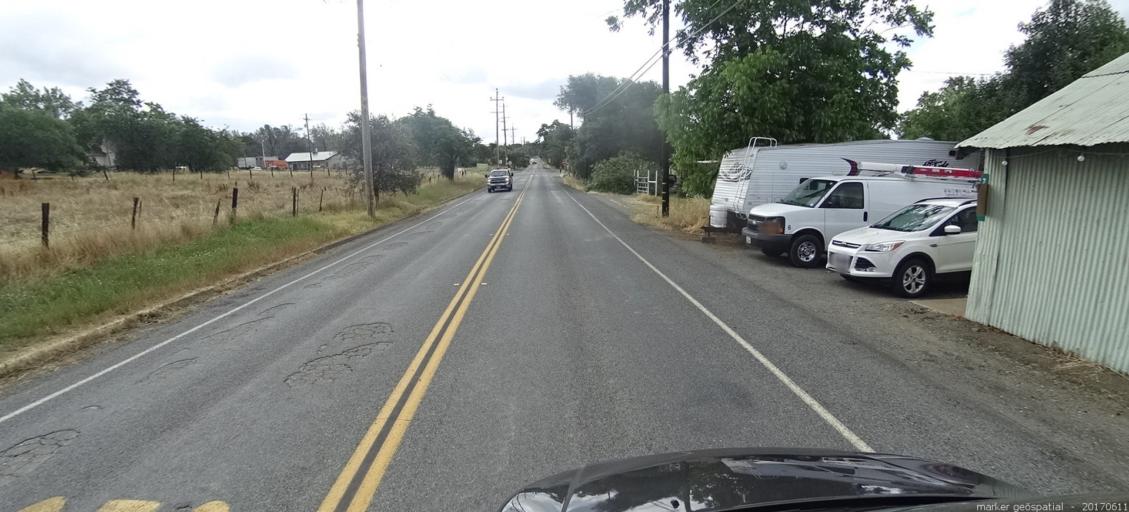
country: US
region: California
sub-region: Yuba County
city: Loma Rica
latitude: 39.3893
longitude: -121.4065
